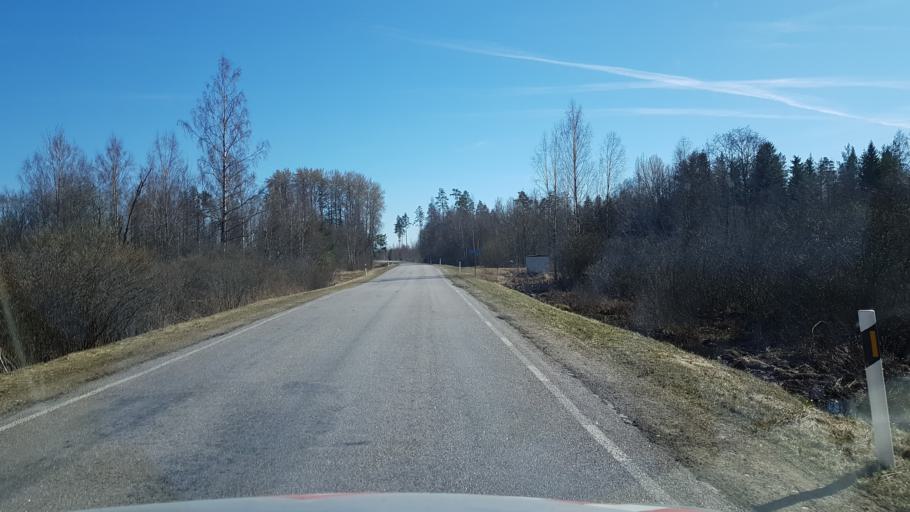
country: EE
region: Laeaene-Virumaa
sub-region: Vinni vald
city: Vinni
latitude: 59.2491
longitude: 26.6883
